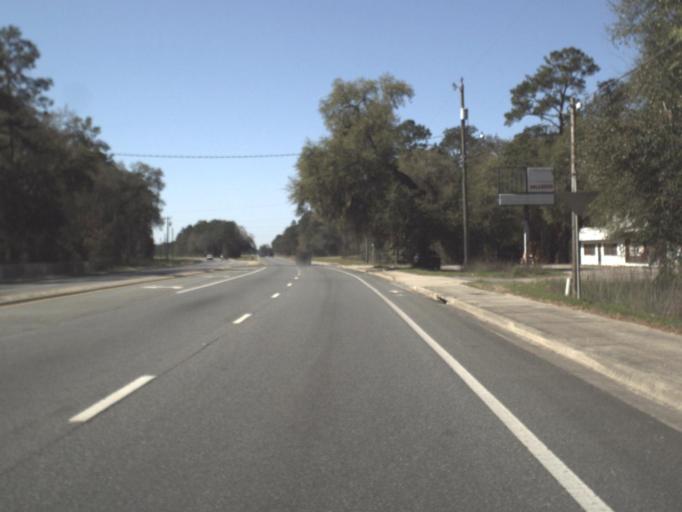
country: US
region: Florida
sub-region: Leon County
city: Woodville
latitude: 30.3571
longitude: -84.3038
